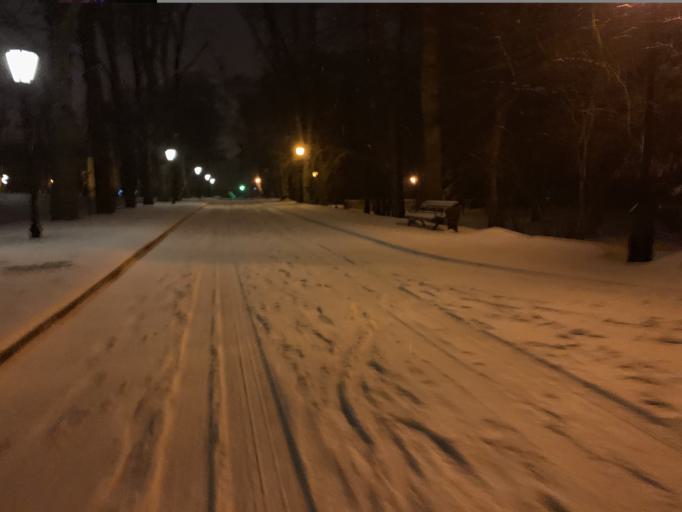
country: BY
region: Minsk
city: Nyasvizh
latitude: 53.2235
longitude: 26.6926
